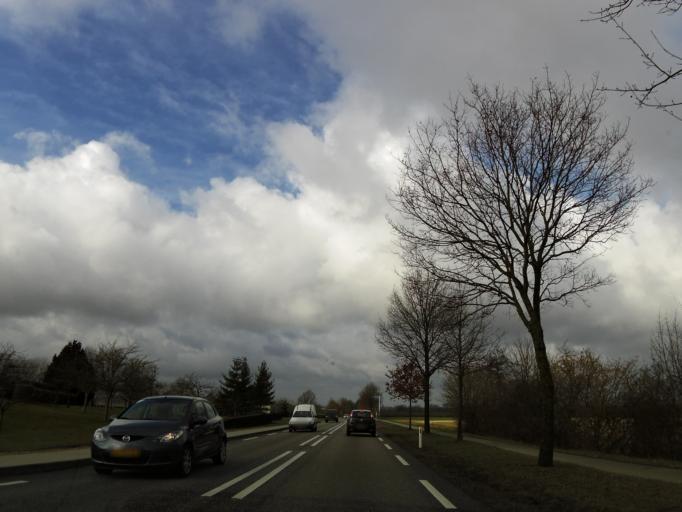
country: NL
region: Limburg
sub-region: Eijsden-Margraten
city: Margraten
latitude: 50.8209
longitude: 5.8054
